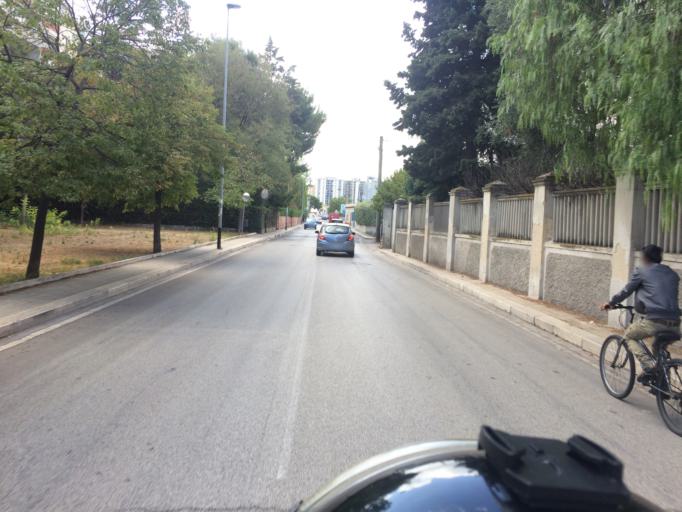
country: IT
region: Apulia
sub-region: Provincia di Bari
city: Bari
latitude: 41.1054
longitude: 16.8584
